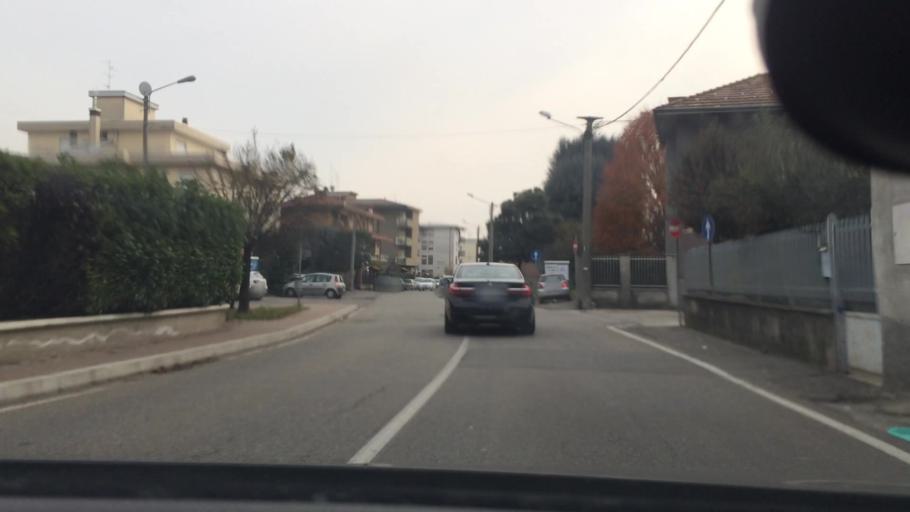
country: IT
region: Lombardy
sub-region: Provincia di Monza e Brianza
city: Cogliate
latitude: 45.6430
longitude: 9.0799
